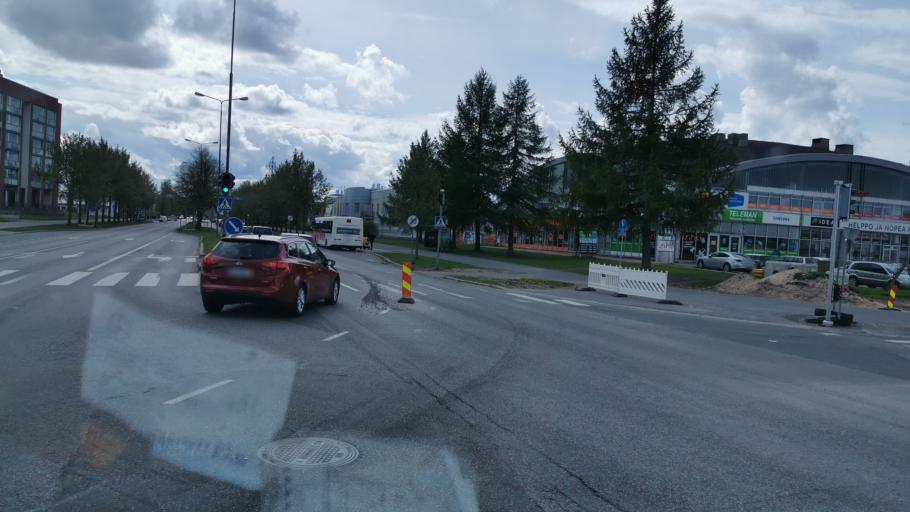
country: FI
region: Northern Ostrobothnia
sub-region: Oulu
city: Oulu
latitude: 65.0007
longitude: 25.4638
